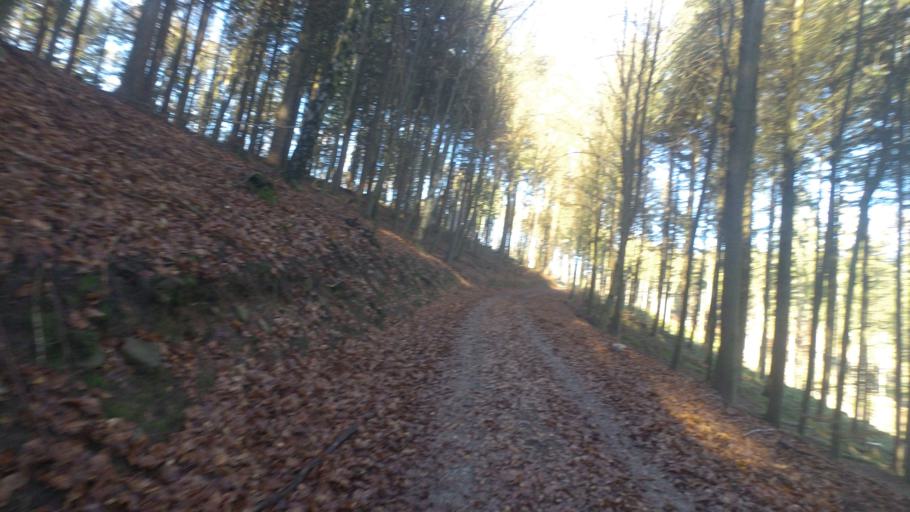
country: DE
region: Baden-Wuerttemberg
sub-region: Karlsruhe Region
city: Heiligkreuzsteinach
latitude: 49.4948
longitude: 8.8047
